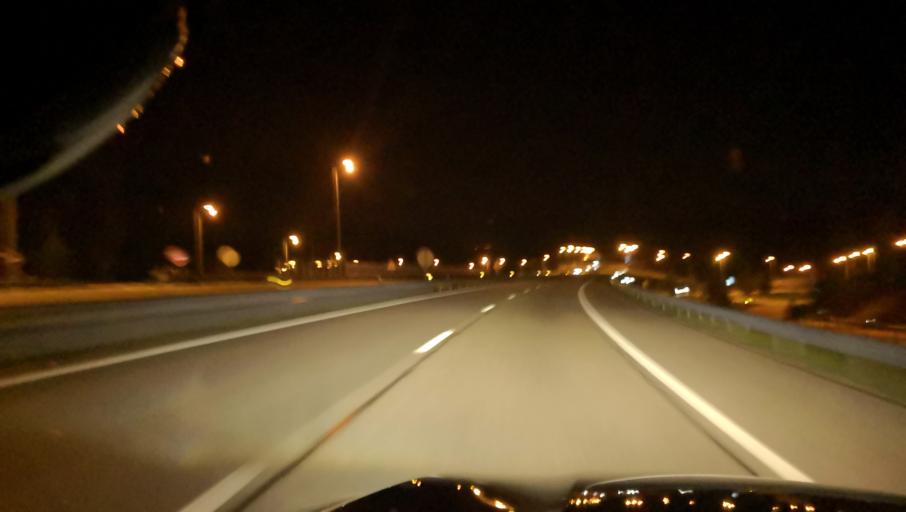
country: PT
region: Viseu
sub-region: Oliveira de Frades
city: Oliveira de Frades
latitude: 40.6825
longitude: -8.1971
